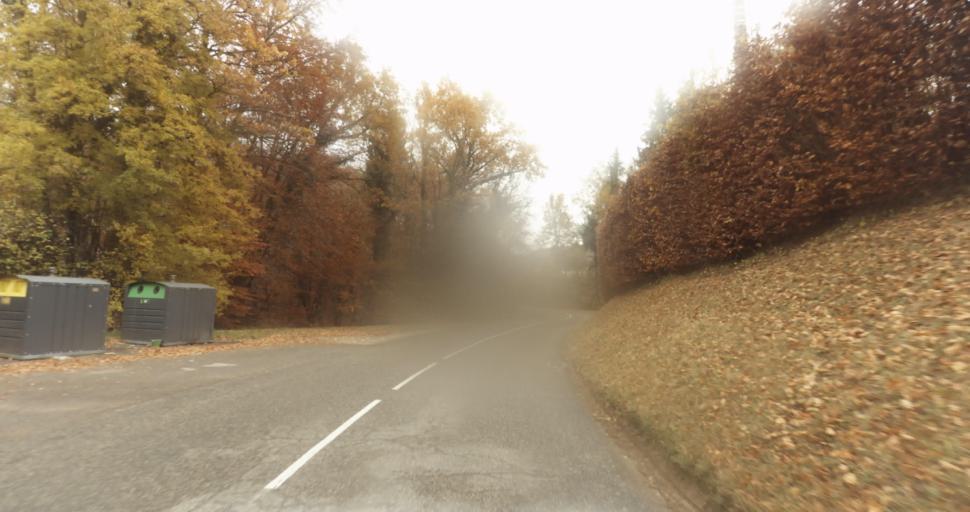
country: FR
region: Rhone-Alpes
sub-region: Departement de la Haute-Savoie
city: Saint-Martin-Bellevue
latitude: 45.9897
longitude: 6.1543
